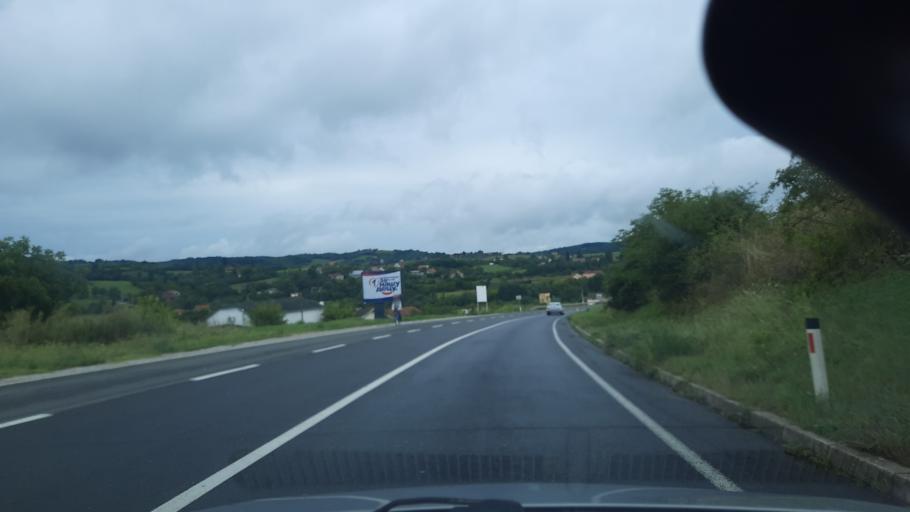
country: RS
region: Central Serbia
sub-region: Sumadijski Okrug
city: Kragujevac
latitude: 43.9781
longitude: 20.8278
